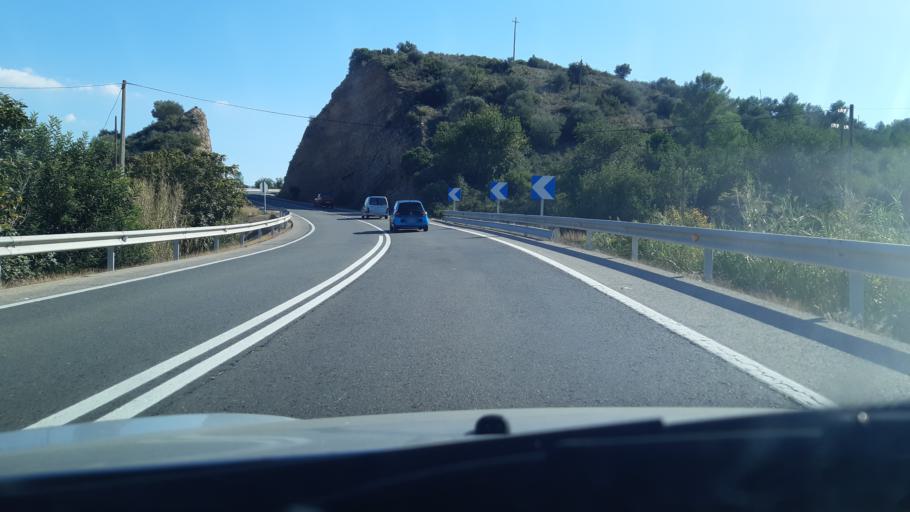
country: ES
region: Catalonia
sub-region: Provincia de Tarragona
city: Tivenys
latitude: 40.8827
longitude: 0.4948
